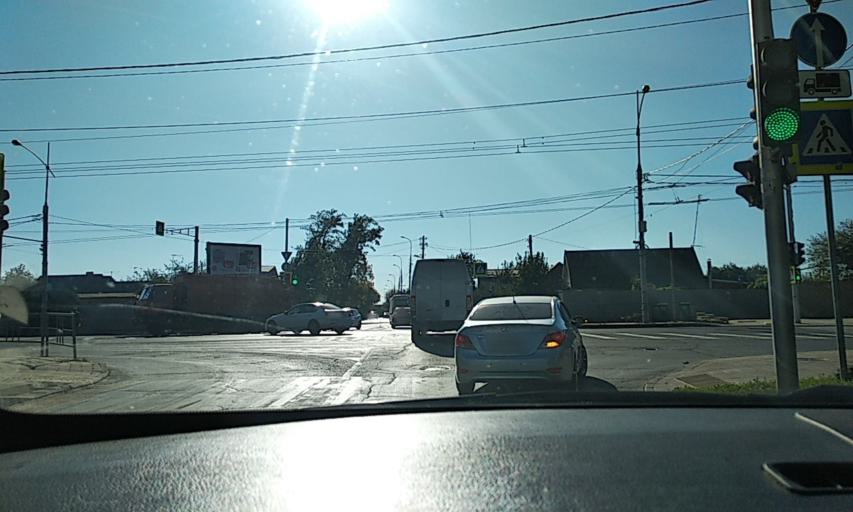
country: RU
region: Krasnodarskiy
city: Pashkovskiy
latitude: 45.0294
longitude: 39.1231
